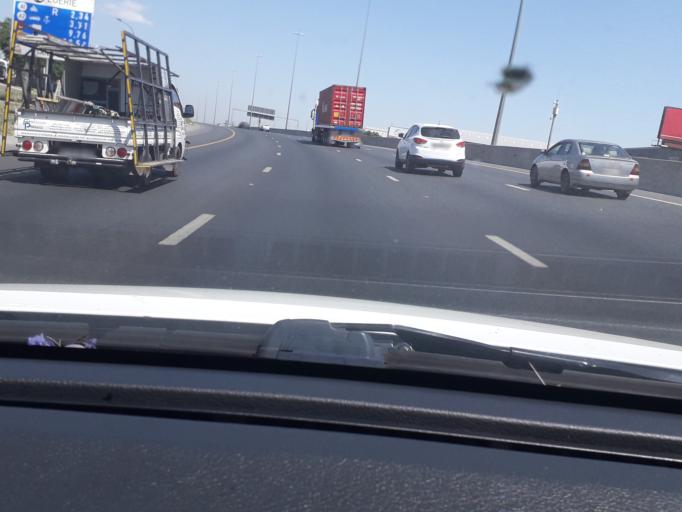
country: ZA
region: Gauteng
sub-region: Ekurhuleni Metropolitan Municipality
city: Germiston
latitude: -26.1663
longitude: 28.1882
